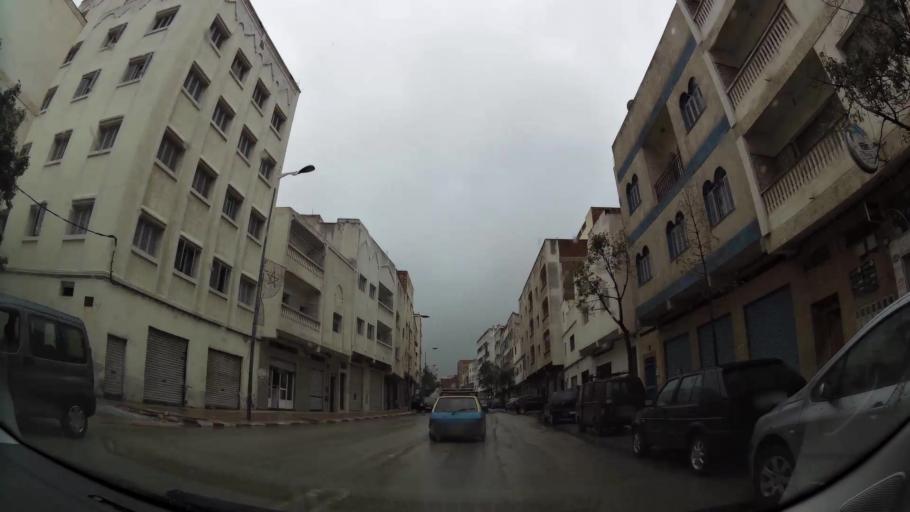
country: MA
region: Taza-Al Hoceima-Taounate
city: Al Hoceima
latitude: 35.2512
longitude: -3.9386
